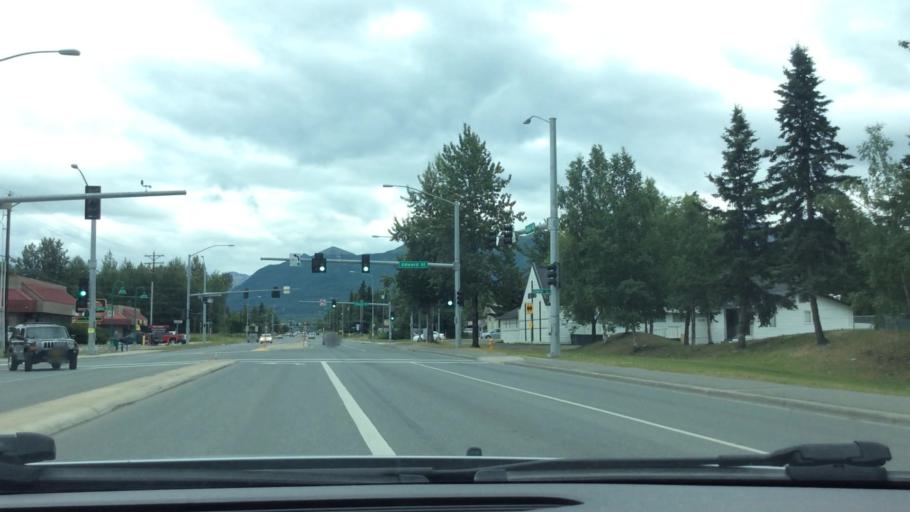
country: US
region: Alaska
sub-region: Anchorage Municipality
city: Anchorage
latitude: 61.2097
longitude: -149.7648
